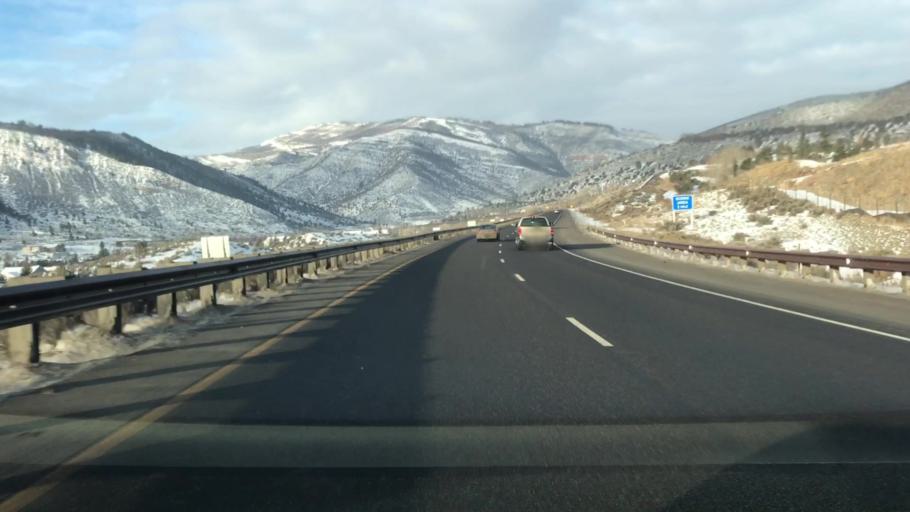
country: US
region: Colorado
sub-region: Eagle County
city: Edwards
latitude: 39.6544
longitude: -106.6117
